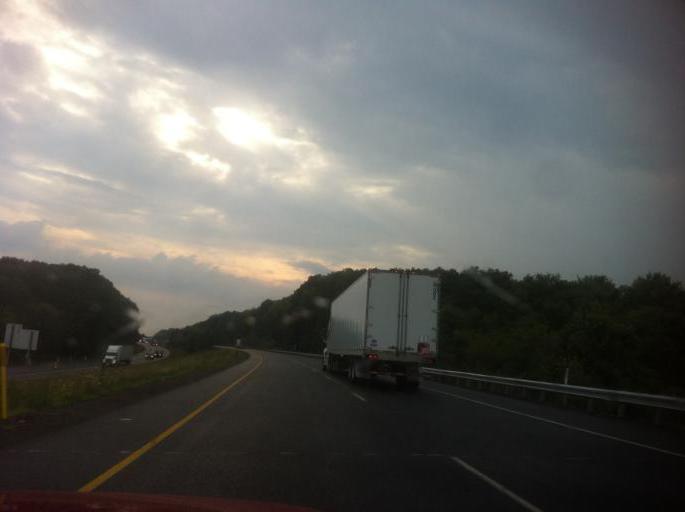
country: US
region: Pennsylvania
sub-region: Clarion County
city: Marianne
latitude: 41.1962
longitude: -79.4404
